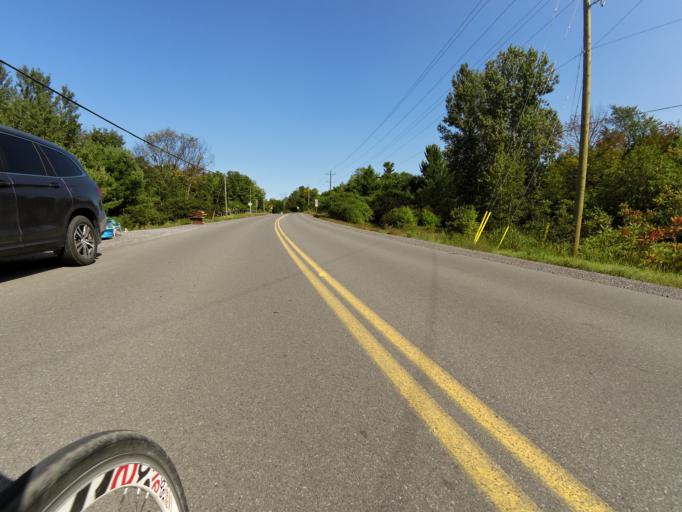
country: CA
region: Ontario
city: Arnprior
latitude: 45.4374
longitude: -76.1143
